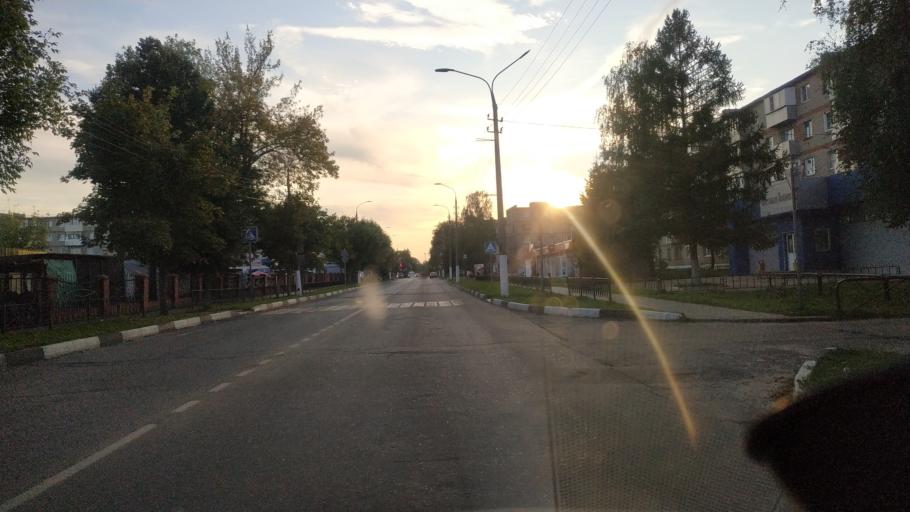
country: RU
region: Moskovskaya
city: Roshal'
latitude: 55.6633
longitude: 39.8553
